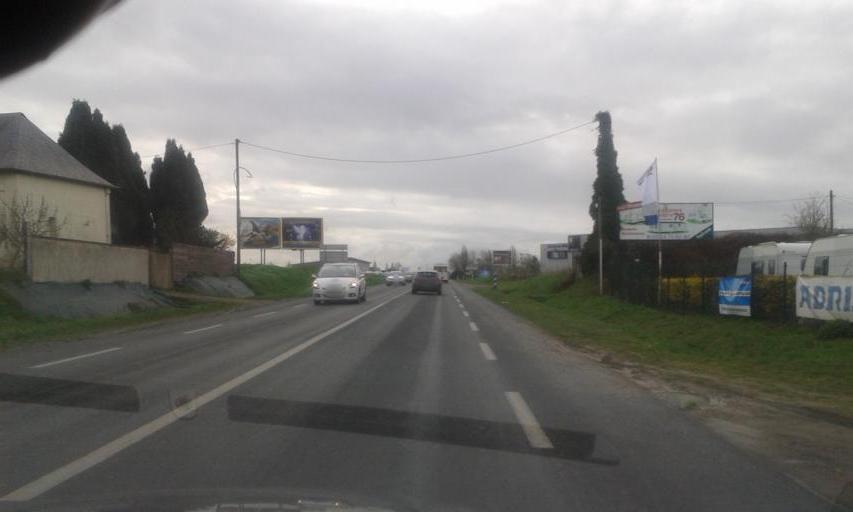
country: FR
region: Haute-Normandie
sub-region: Departement de la Seine-Maritime
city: Boos
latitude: 49.3929
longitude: 1.1906
